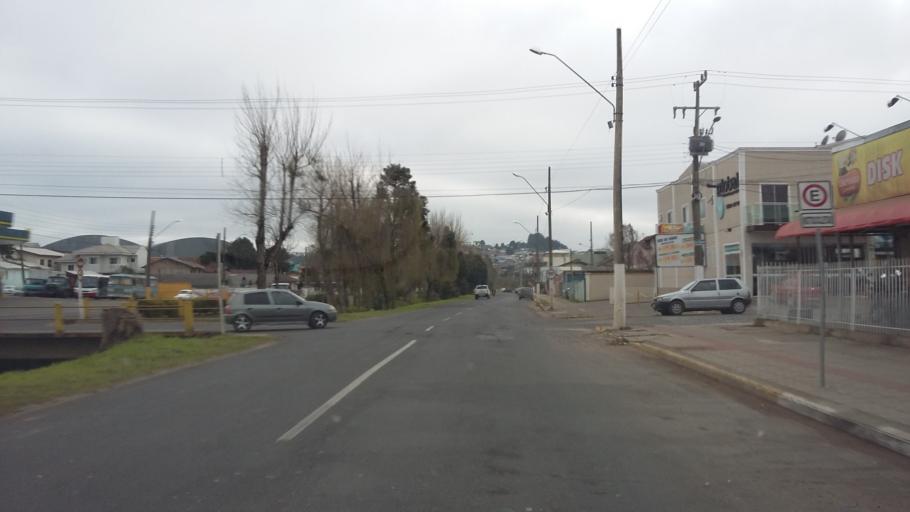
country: BR
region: Santa Catarina
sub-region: Lages
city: Lages
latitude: -27.8196
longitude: -50.3387
